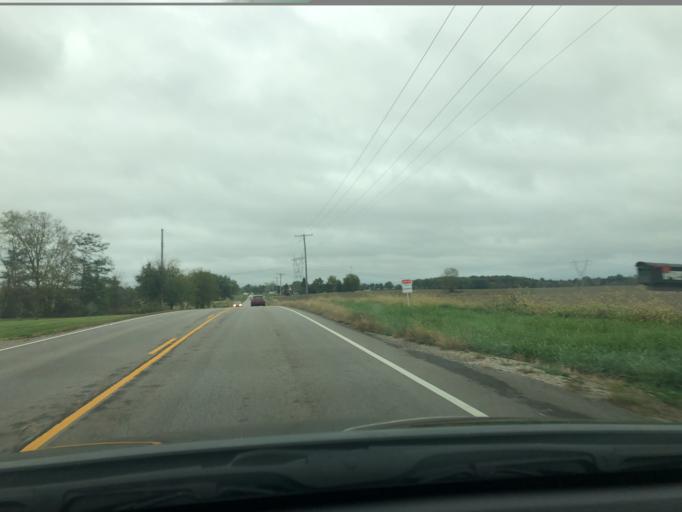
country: US
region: Ohio
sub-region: Union County
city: Marysville
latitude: 40.2560
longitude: -83.2763
